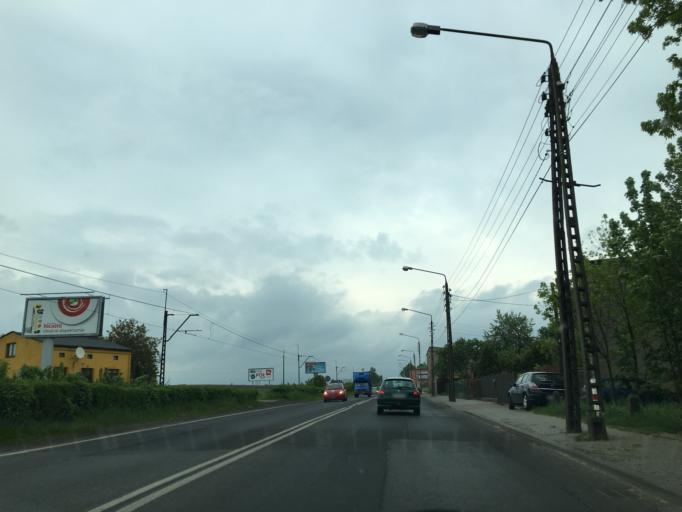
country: PL
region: Silesian Voivodeship
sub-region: Powiat bedzinski
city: Czeladz
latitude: 50.3191
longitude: 19.0824
